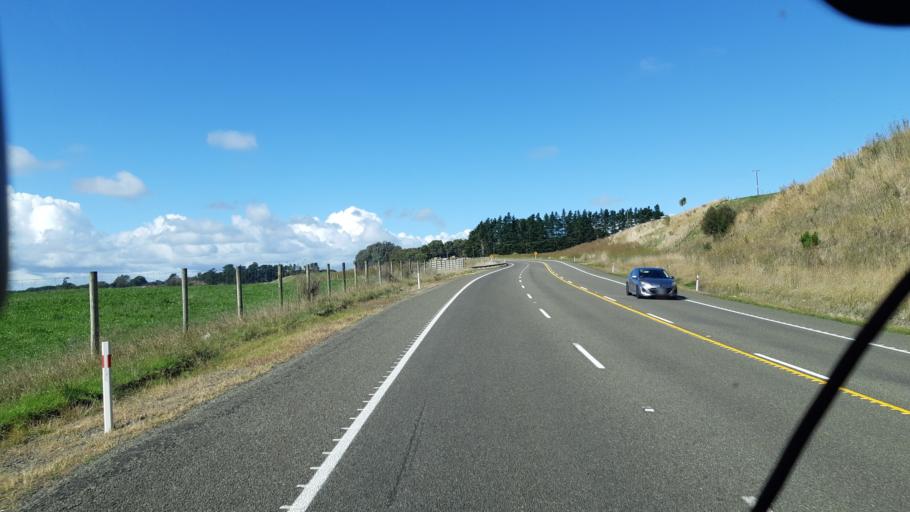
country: NZ
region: Manawatu-Wanganui
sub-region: Wanganui District
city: Wanganui
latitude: -39.9703
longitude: 175.1088
